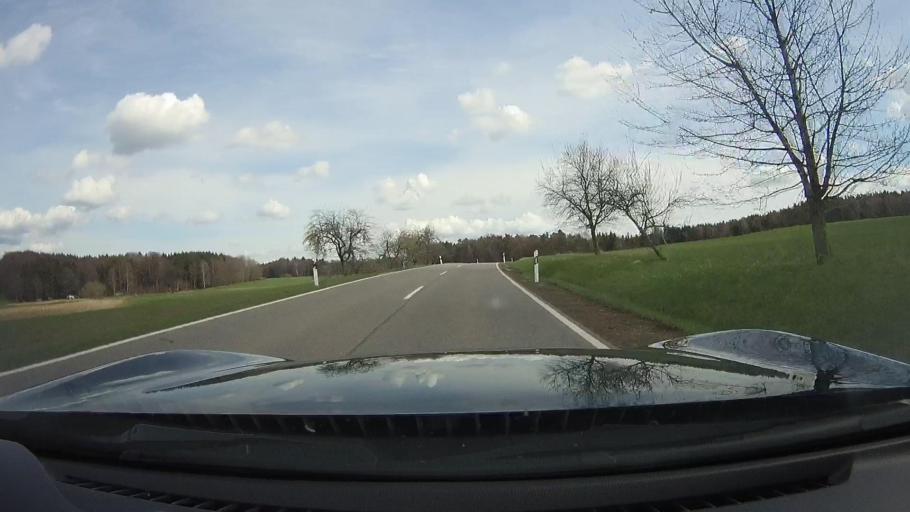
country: DE
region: Baden-Wuerttemberg
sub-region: Karlsruhe Region
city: Mudau
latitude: 49.5406
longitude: 9.1611
